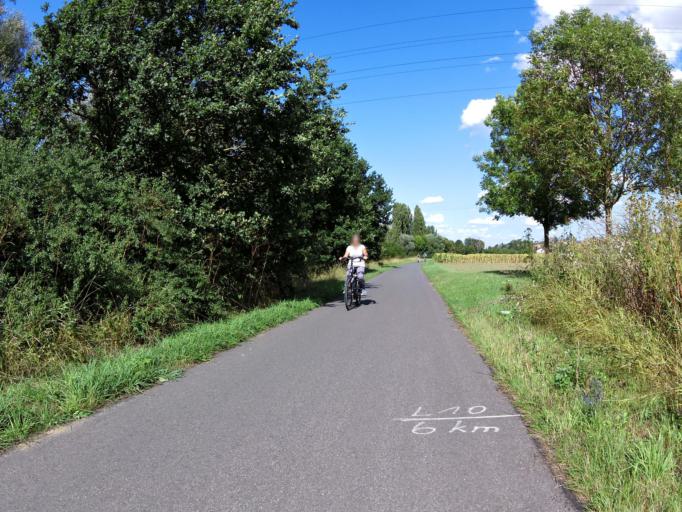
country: DE
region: Bavaria
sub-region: Regierungsbezirk Unterfranken
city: Sulzfeld am Main
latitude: 49.7142
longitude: 10.1450
